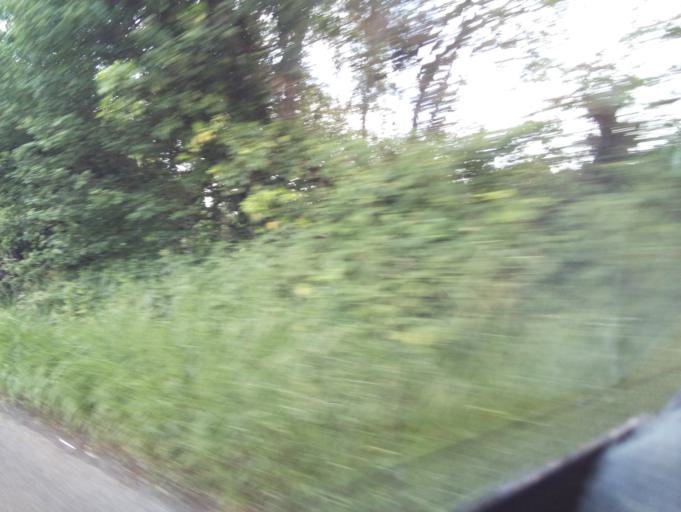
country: GB
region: England
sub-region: South Gloucestershire
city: Bitton
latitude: 51.4169
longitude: -2.4410
